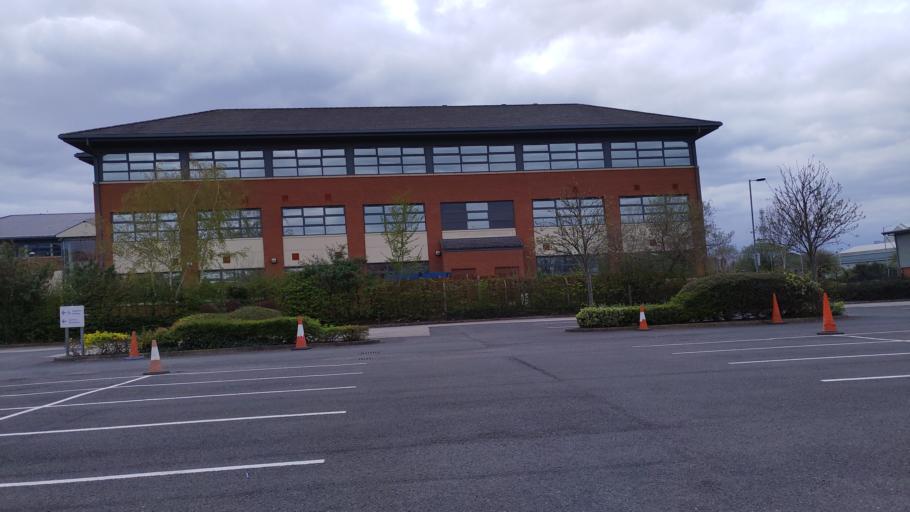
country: GB
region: England
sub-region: Lancashire
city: Preston
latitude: 53.7601
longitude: -2.7182
